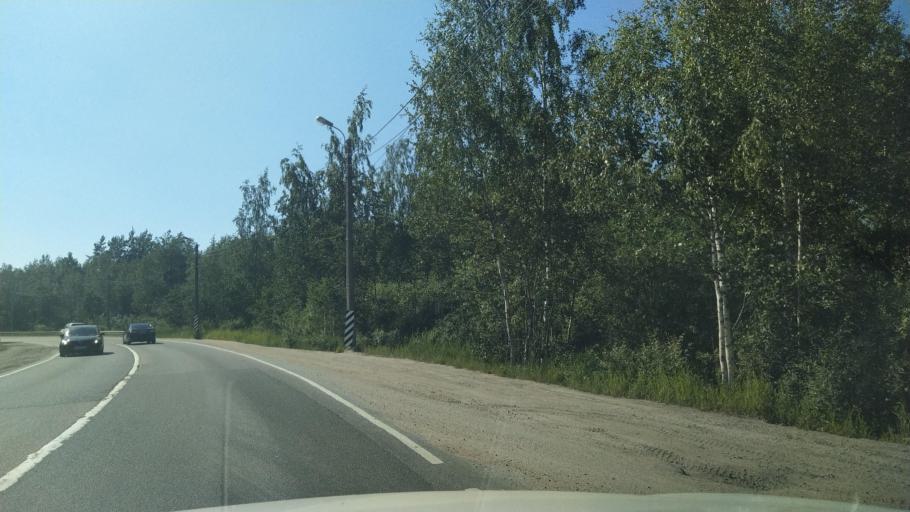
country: RU
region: St.-Petersburg
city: Beloostrov
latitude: 60.1467
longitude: 29.9946
